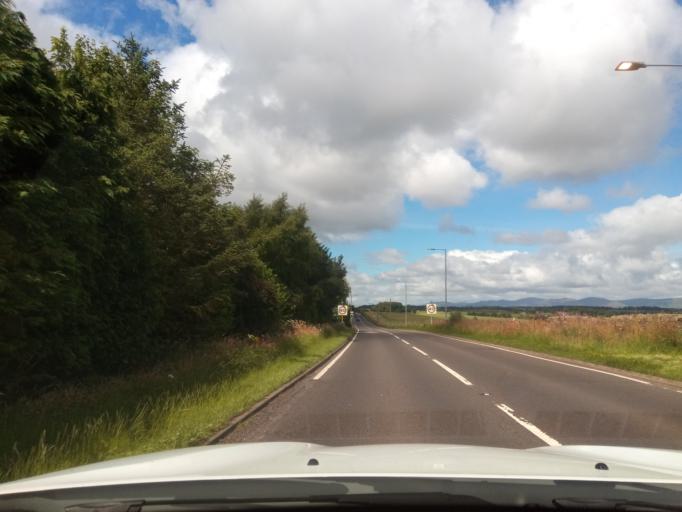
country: GB
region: Scotland
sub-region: Fife
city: Cairneyhill
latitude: 56.0483
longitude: -3.5243
